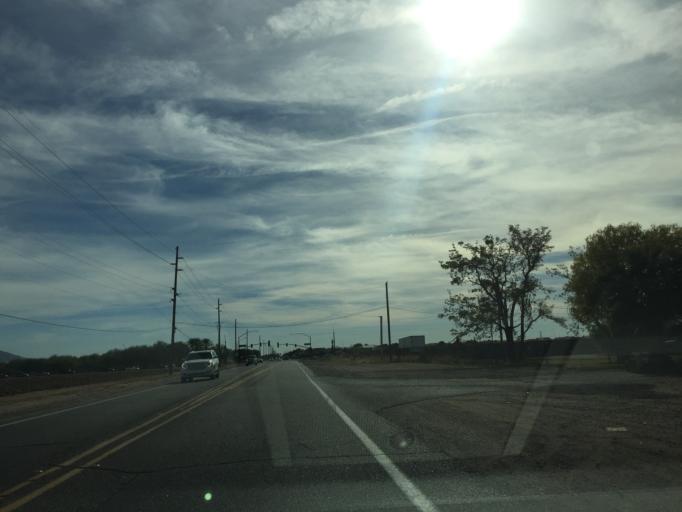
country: US
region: Arizona
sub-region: Maricopa County
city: Chandler
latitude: 33.2797
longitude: -111.7728
